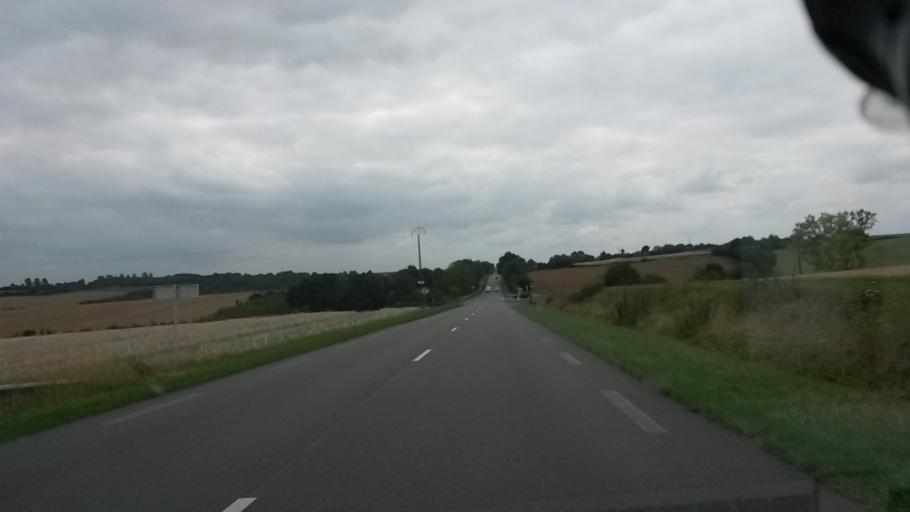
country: FR
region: Picardie
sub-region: Departement de la Somme
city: Corbie
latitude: 49.9759
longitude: 2.5601
